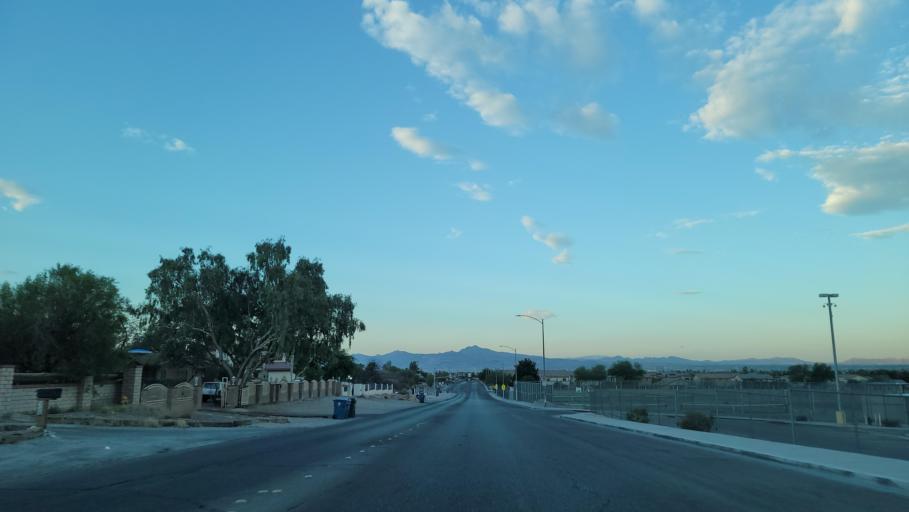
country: US
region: Nevada
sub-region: Clark County
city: Sunrise Manor
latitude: 36.1659
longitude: -115.0353
